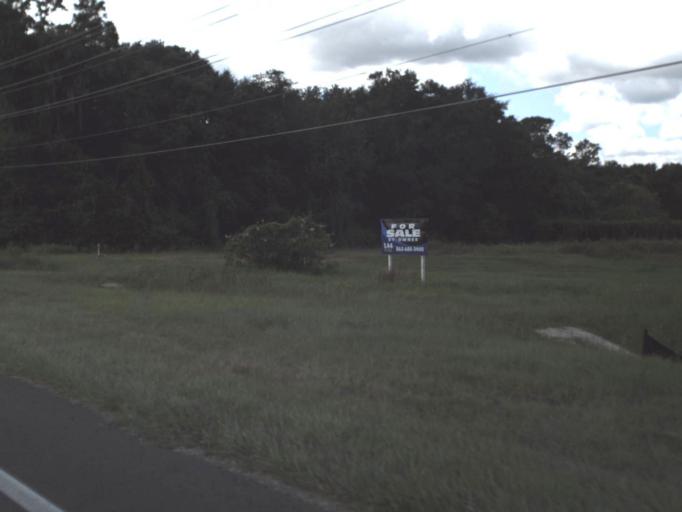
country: US
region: Florida
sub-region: Polk County
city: Gibsonia
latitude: 28.1581
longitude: -81.9738
